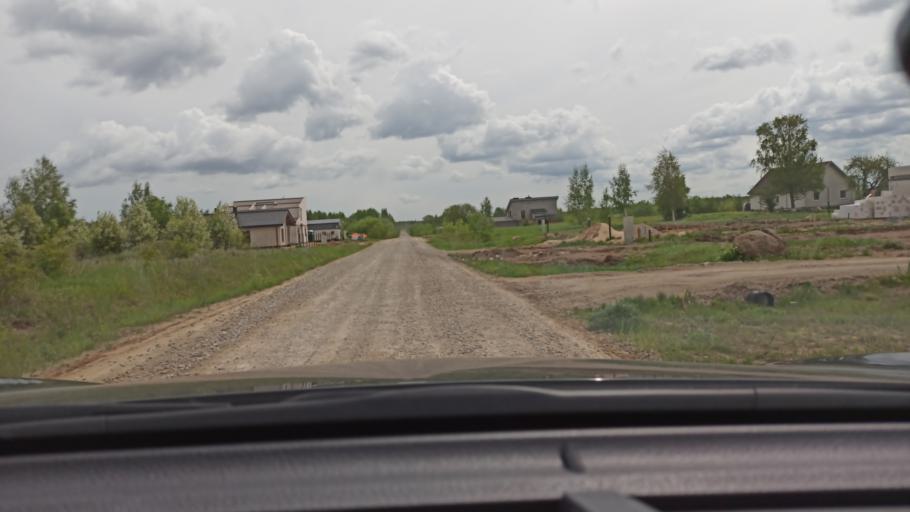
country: LT
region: Siauliu apskritis
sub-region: Siauliai
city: Siauliai
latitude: 55.9008
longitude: 23.3073
